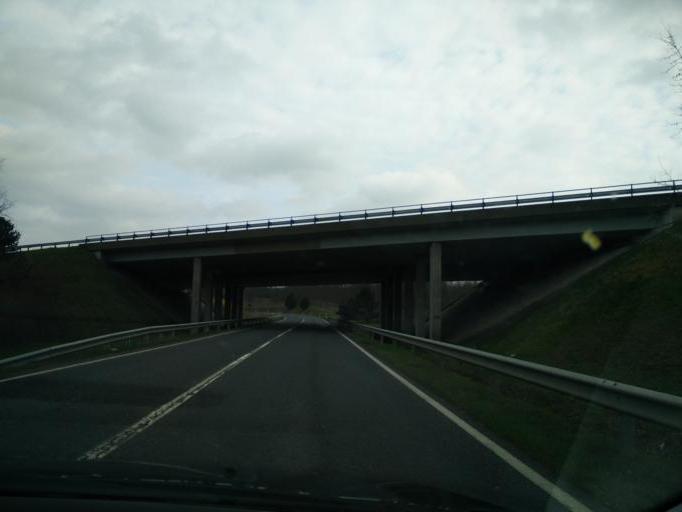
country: HU
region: Gyor-Moson-Sopron
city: Per
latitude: 47.6866
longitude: 17.8039
